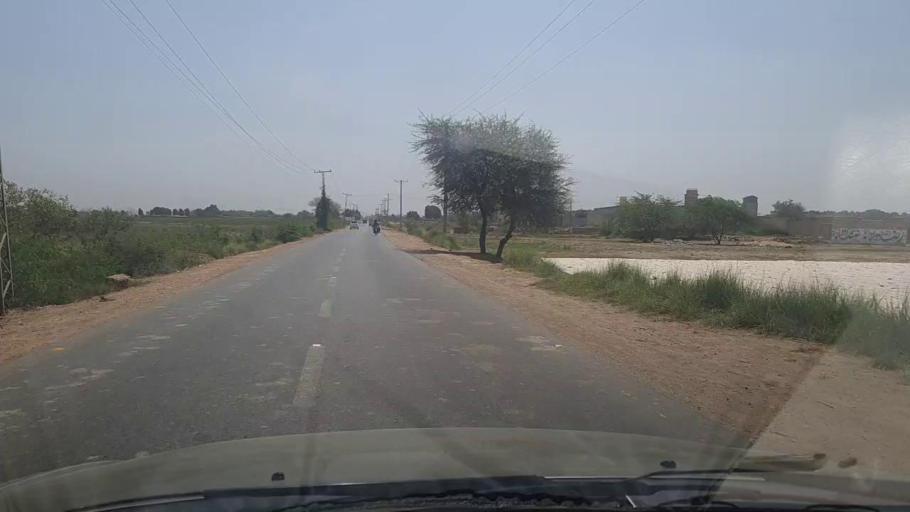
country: PK
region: Sindh
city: Hyderabad
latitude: 25.3901
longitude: 68.4130
